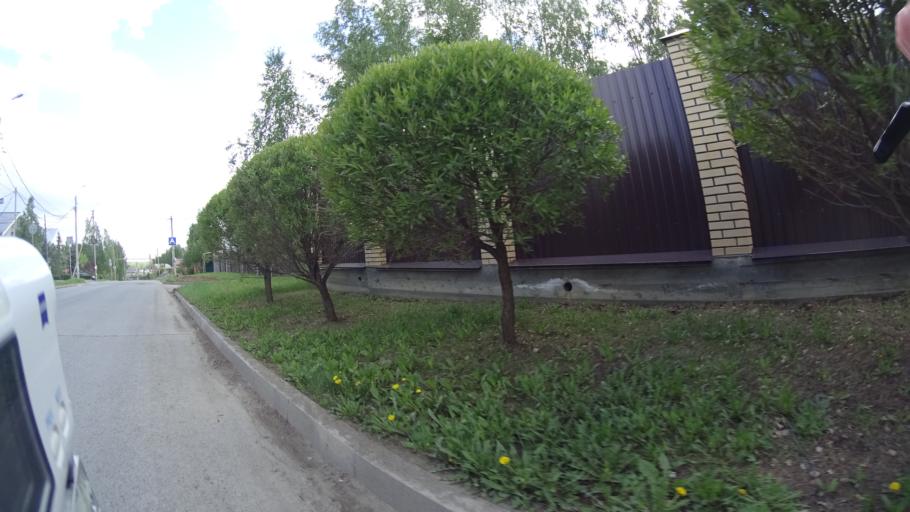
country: RU
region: Chelyabinsk
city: Sargazy
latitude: 55.1584
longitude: 61.2518
